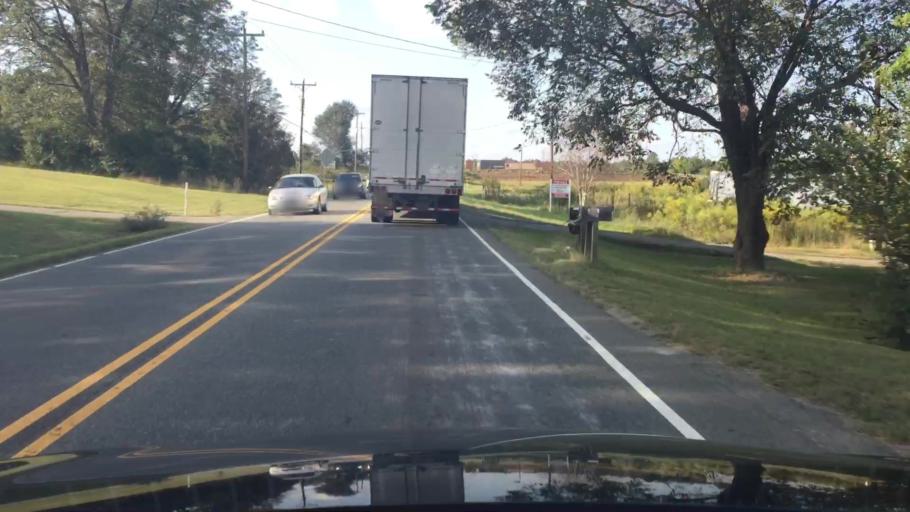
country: US
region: North Carolina
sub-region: Iredell County
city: Troutman
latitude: 35.6666
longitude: -80.8520
